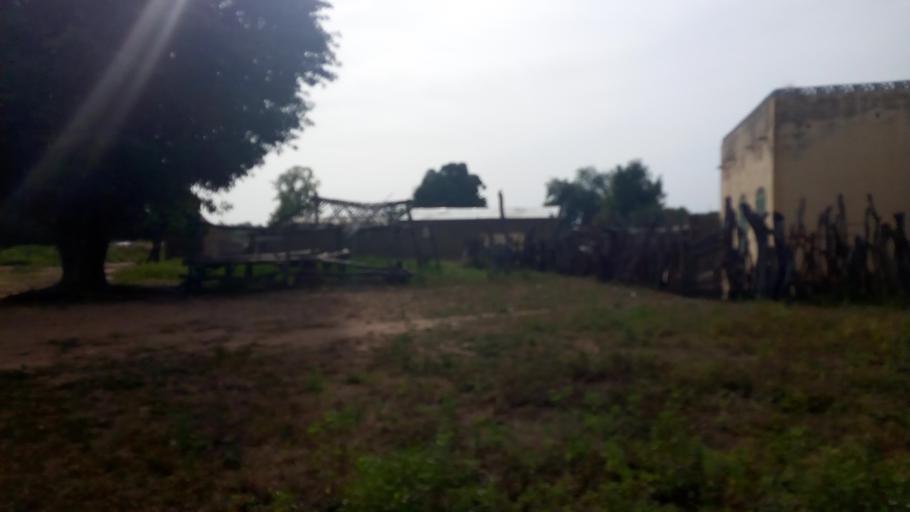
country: ML
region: Kayes
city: Kita
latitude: 13.1419
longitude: -8.8661
